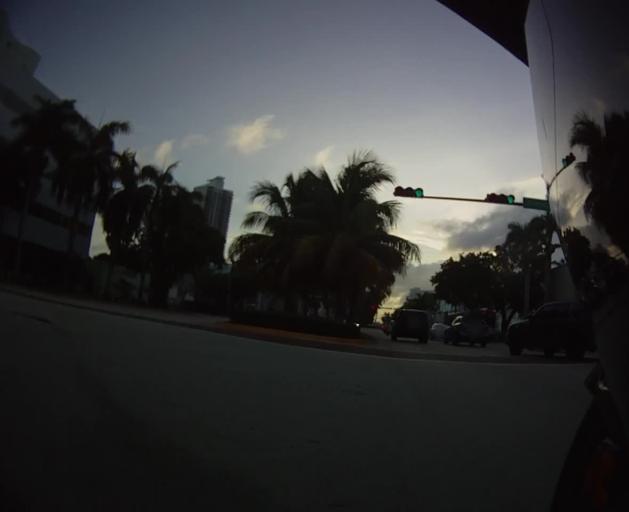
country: US
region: Florida
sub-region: Miami-Dade County
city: Miami Beach
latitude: 25.7745
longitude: -80.1371
